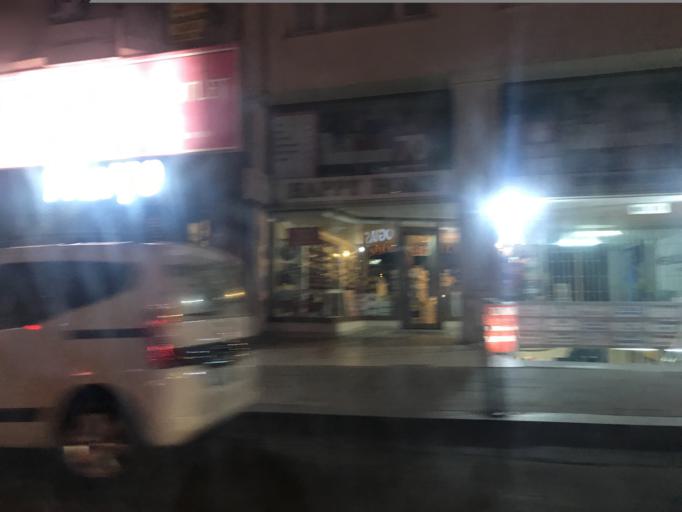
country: TR
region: Istanbul
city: Maltepe
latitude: 40.9221
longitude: 29.1353
